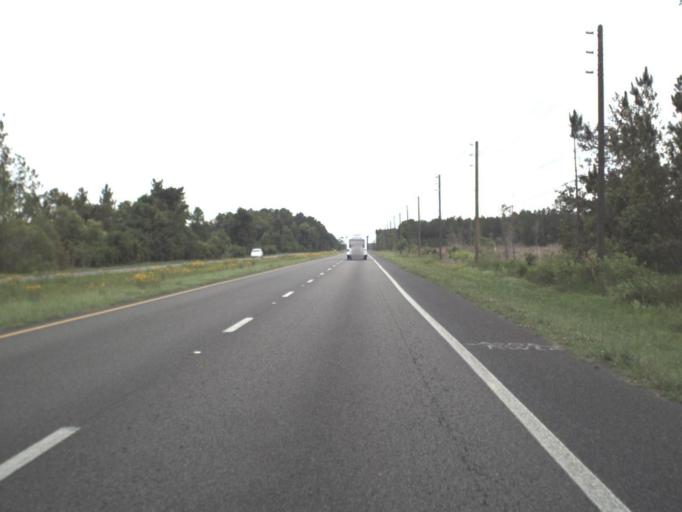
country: US
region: Florida
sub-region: Nassau County
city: Callahan
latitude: 30.6003
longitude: -81.8337
